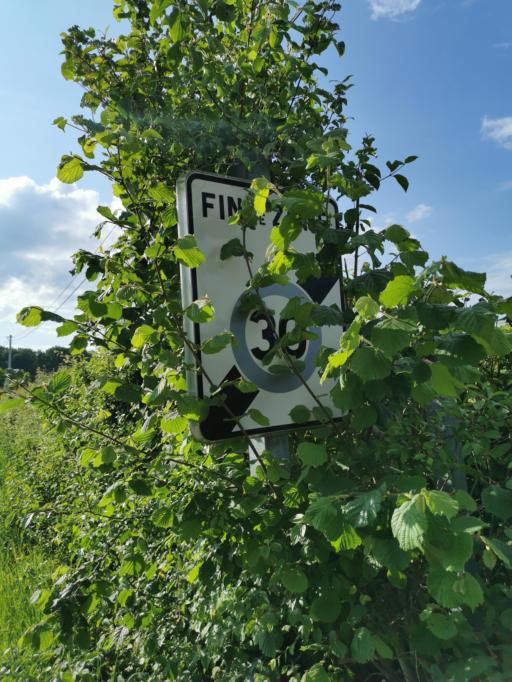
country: FR
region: Nord-Pas-de-Calais
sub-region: Departement du Nord
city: Anor
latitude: 49.9818
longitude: 4.0907
